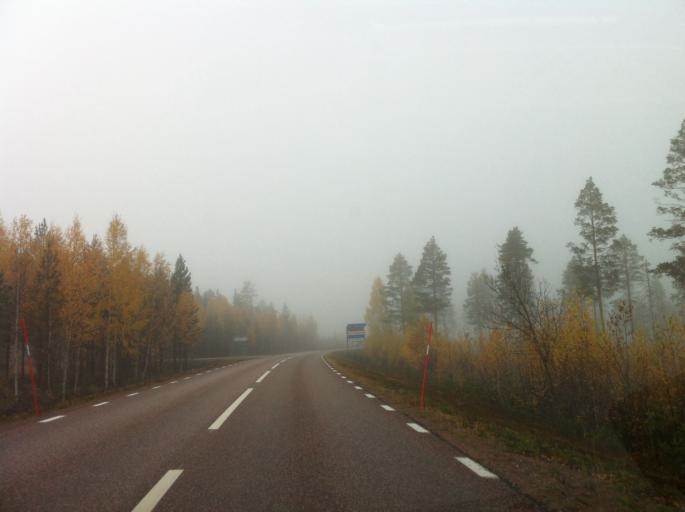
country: NO
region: Hedmark
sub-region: Trysil
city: Innbygda
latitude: 61.6923
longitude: 13.0671
